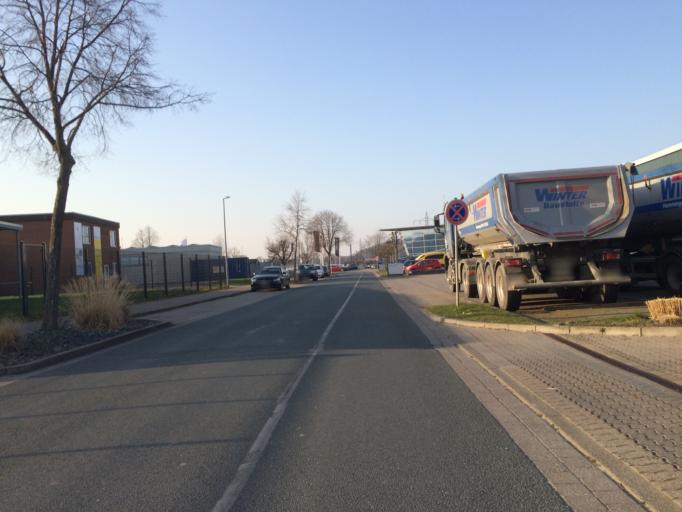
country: DE
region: Lower Saxony
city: Gehrden
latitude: 52.3149
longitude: 9.6145
